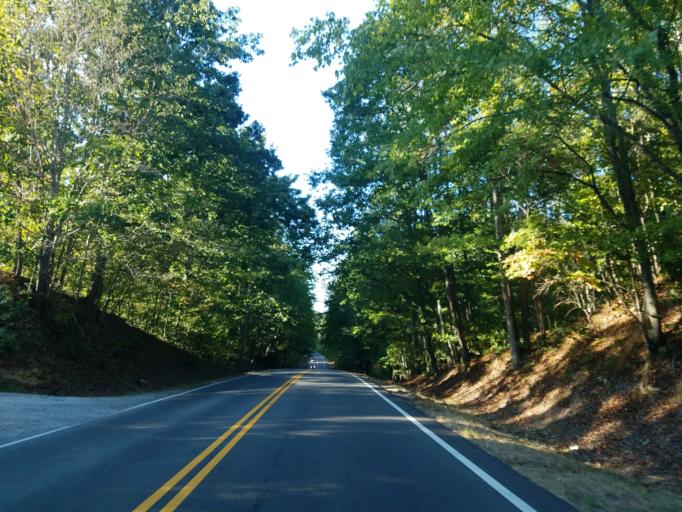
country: US
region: Georgia
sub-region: Bartow County
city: Emerson
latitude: 34.0752
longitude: -84.8303
